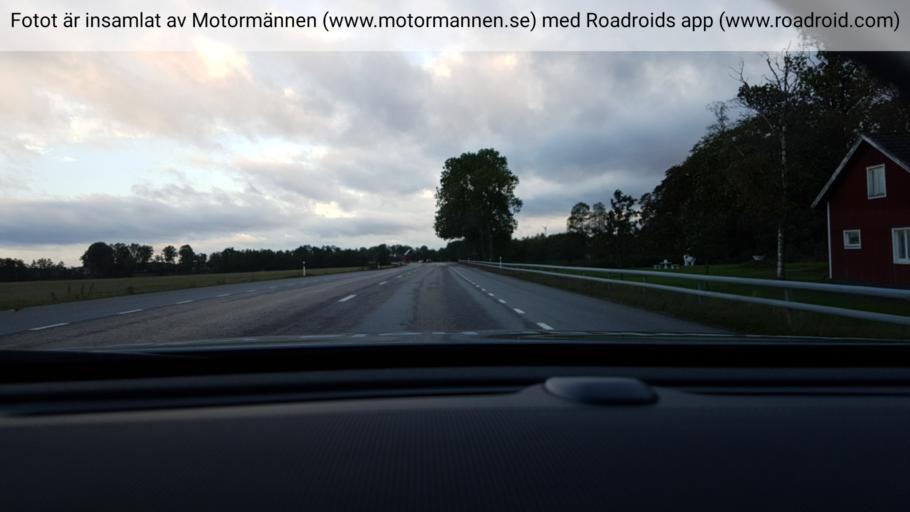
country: SE
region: Vaestra Goetaland
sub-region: Vanersborgs Kommun
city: Bralanda
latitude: 58.5960
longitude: 12.4100
